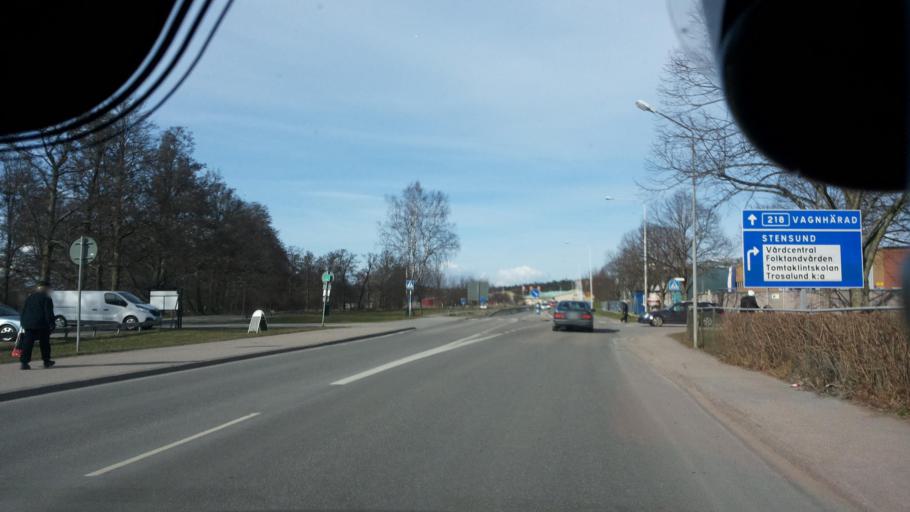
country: SE
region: Soedermanland
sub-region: Trosa Kommun
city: Trosa
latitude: 58.9021
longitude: 17.5490
